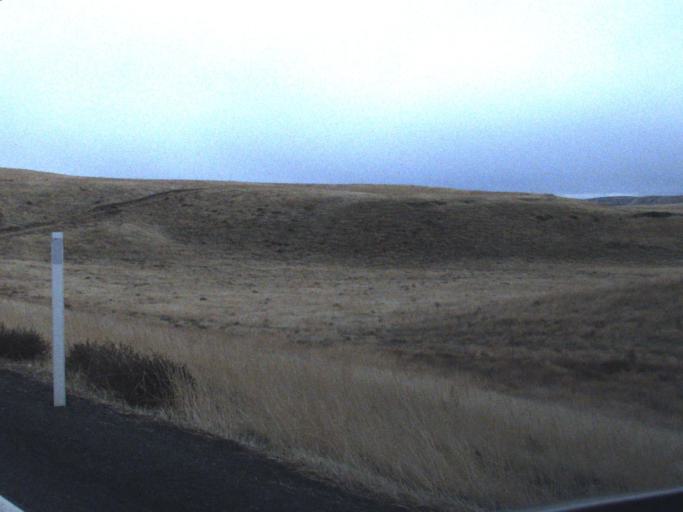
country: US
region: Washington
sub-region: Walla Walla County
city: Burbank
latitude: 46.0681
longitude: -118.7627
